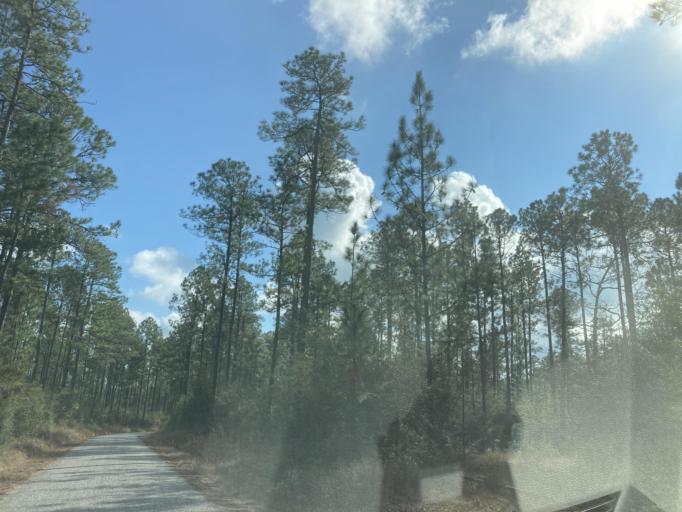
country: US
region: Mississippi
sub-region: Harrison County
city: Saucier
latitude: 30.7052
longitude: -89.2075
